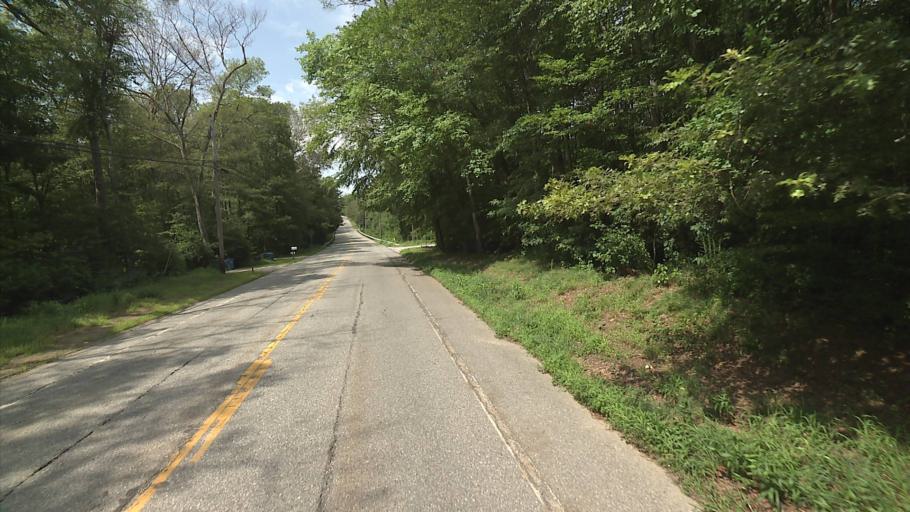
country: US
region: Connecticut
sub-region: New London County
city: Colchester
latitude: 41.5389
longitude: -72.2711
